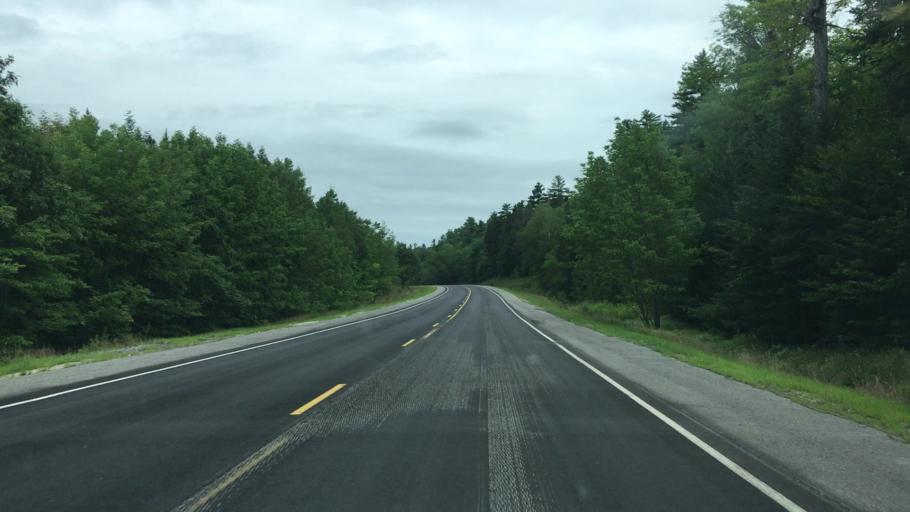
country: US
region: Maine
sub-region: Washington County
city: Cherryfield
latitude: 44.8964
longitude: -67.8558
